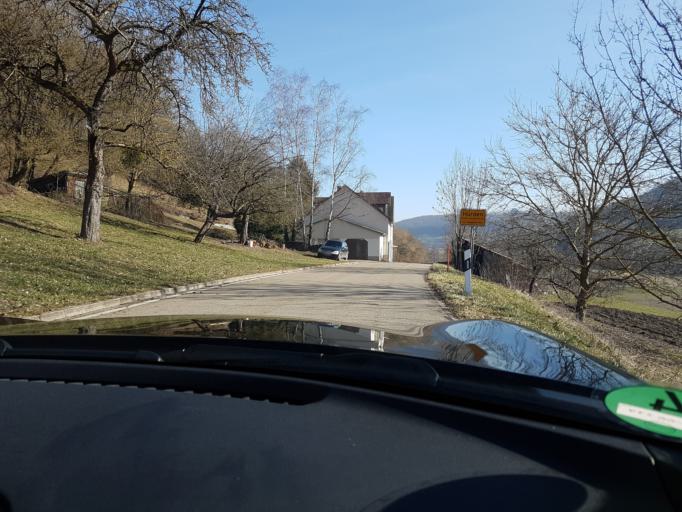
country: DE
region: Baden-Wuerttemberg
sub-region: Regierungsbezirk Stuttgart
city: Langenburg
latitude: 49.2303
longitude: 9.8596
